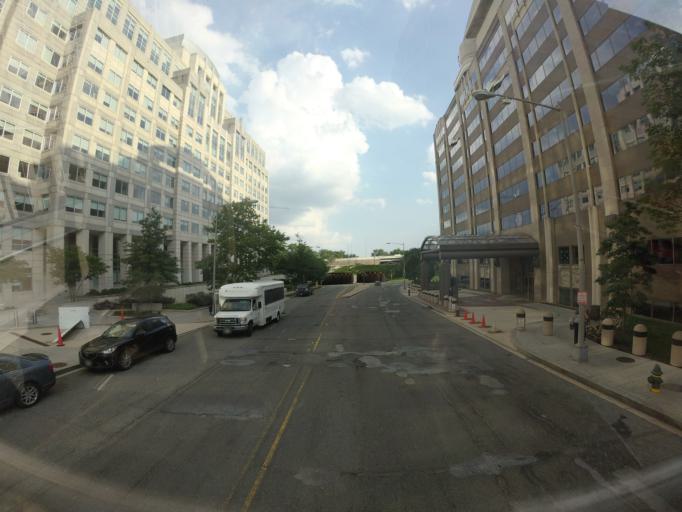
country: US
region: Washington, D.C.
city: Washington, D.C.
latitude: 38.8837
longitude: -77.0282
